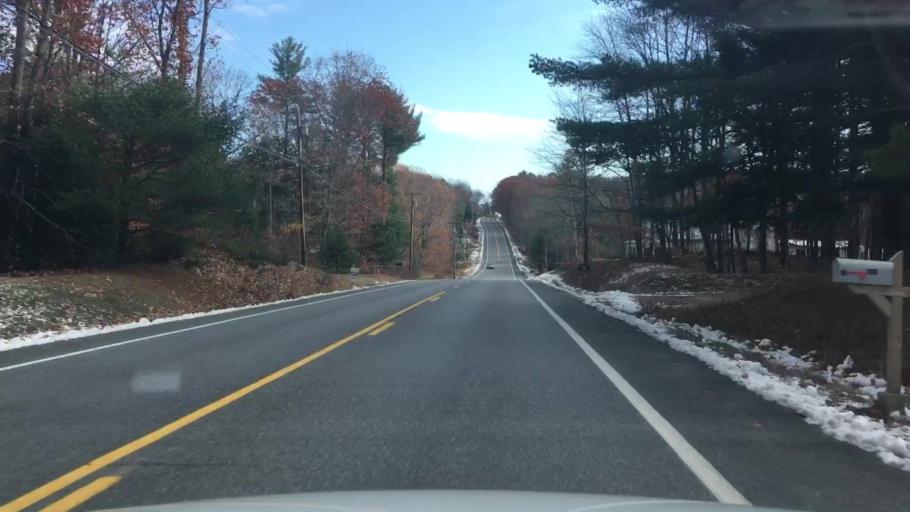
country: US
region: Maine
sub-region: Kennebec County
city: Winthrop
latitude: 44.3252
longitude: -69.9891
